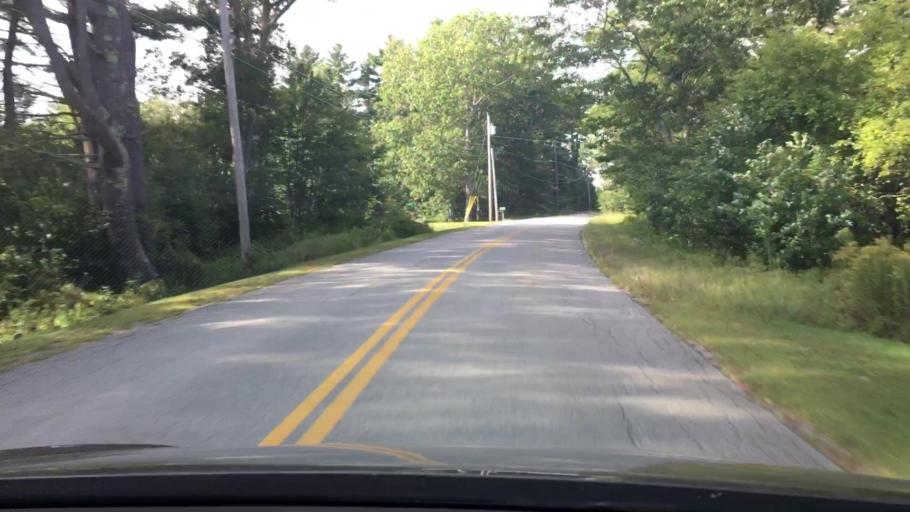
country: US
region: Maine
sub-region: Hancock County
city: Orland
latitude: 44.5229
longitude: -68.7642
